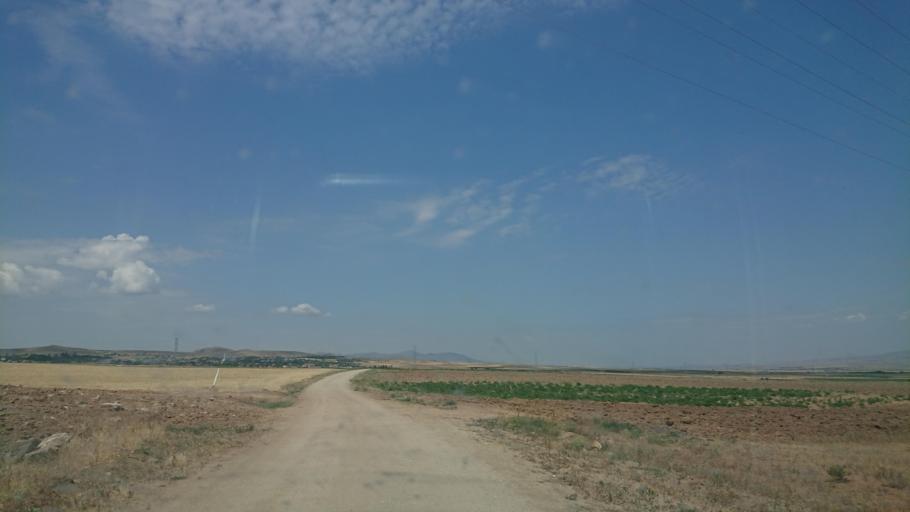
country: TR
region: Aksaray
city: Sariyahsi
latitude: 38.9570
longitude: 33.9128
